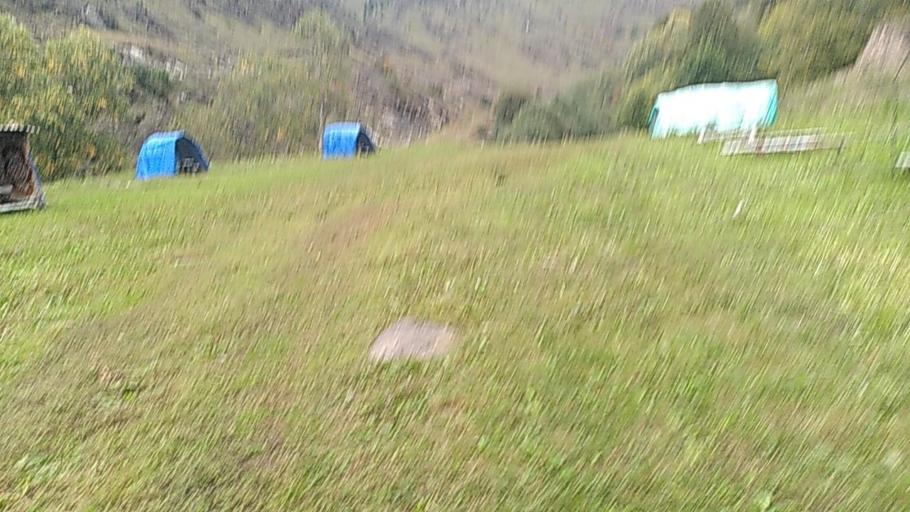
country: RU
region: Kabardino-Balkariya
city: Kamennomostskoye
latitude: 43.7193
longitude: 42.8432
